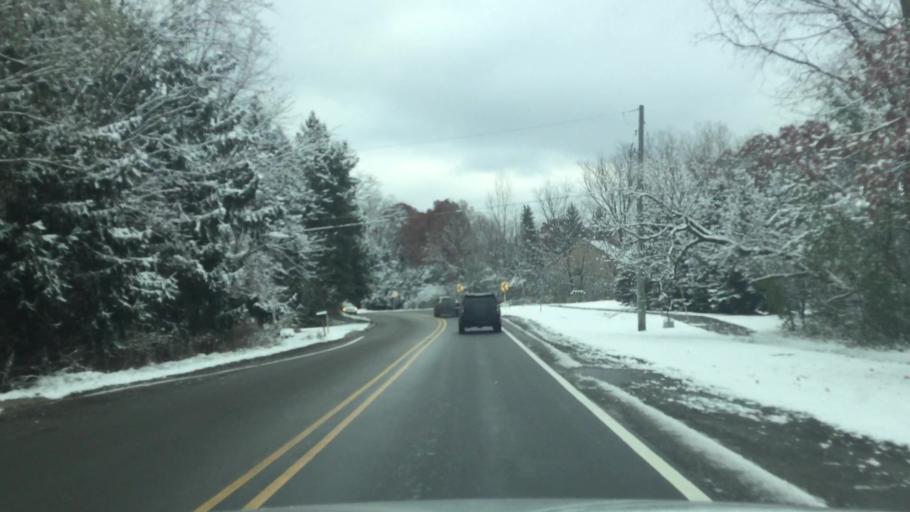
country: US
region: Michigan
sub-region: Oakland County
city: West Bloomfield Township
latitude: 42.5685
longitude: -83.4165
